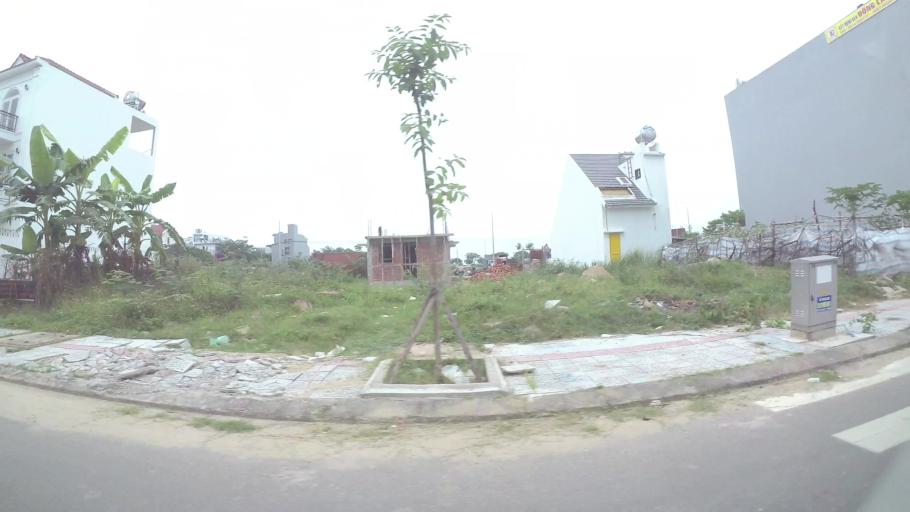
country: VN
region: Da Nang
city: Lien Chieu
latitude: 16.0753
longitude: 108.1611
